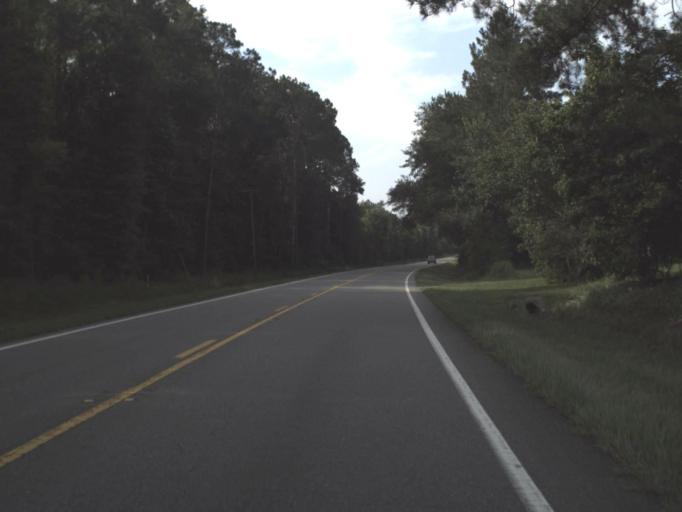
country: US
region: Florida
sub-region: Taylor County
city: Perry
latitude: 30.3421
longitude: -83.6469
